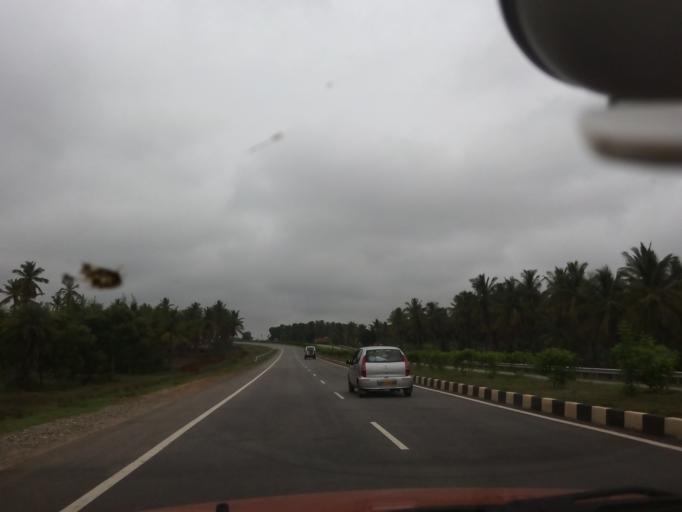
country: IN
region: Karnataka
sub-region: Hassan
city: Shravanabelagola
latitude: 12.9389
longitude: 76.5442
